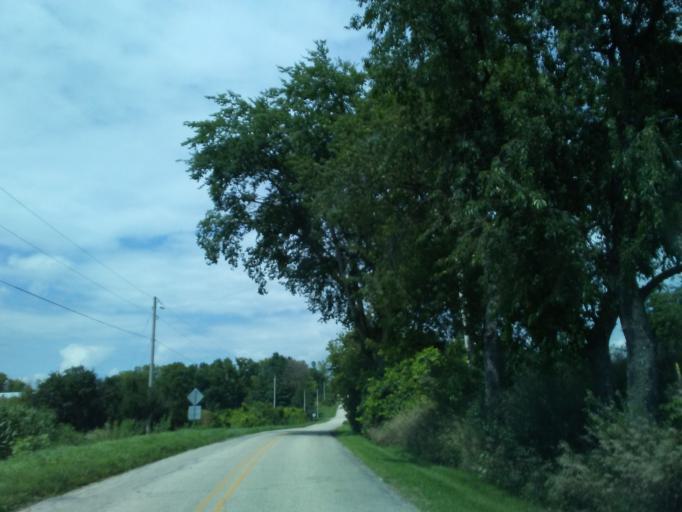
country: US
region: Wisconsin
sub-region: Dane County
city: Verona
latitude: 42.9980
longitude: -89.5780
